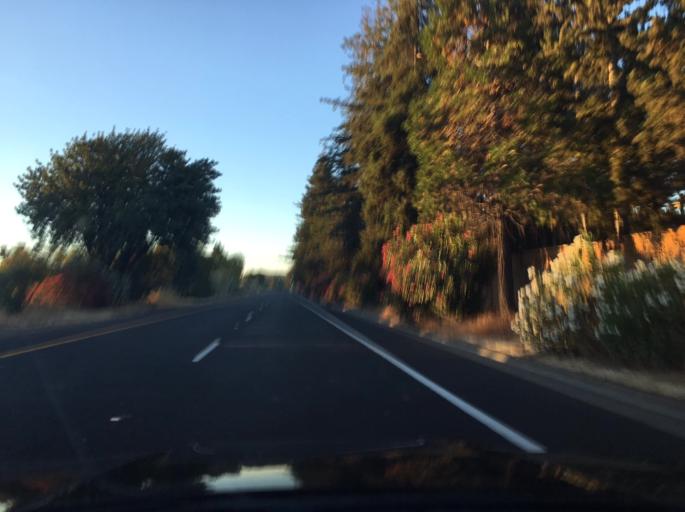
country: US
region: California
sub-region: Santa Clara County
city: Seven Trees
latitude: 37.2181
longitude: -121.8576
